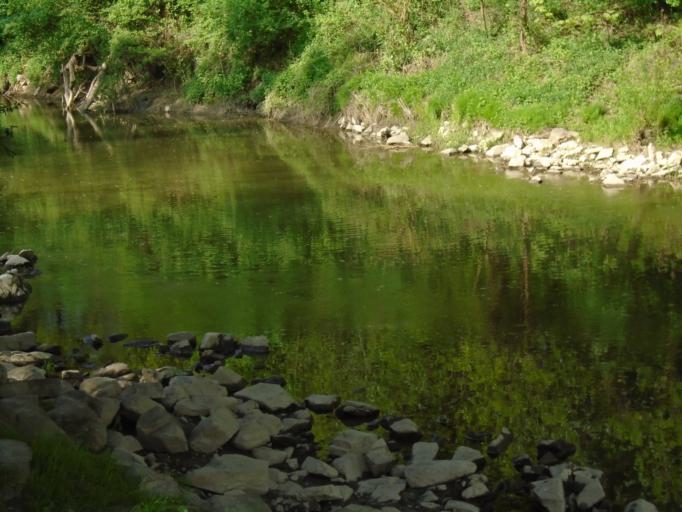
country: CZ
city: Ludgerovice
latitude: 49.8417
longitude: 18.2194
